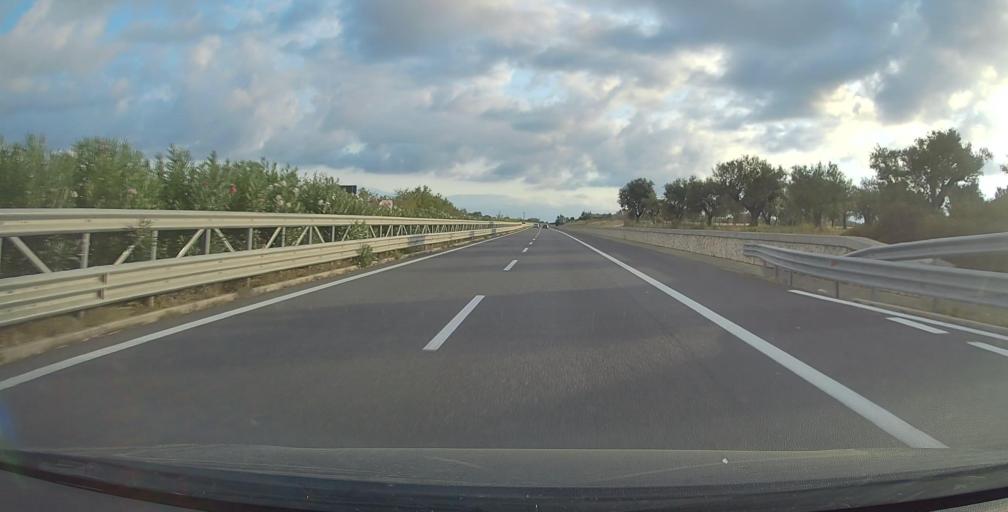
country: IT
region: Calabria
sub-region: Provincia di Catanzaro
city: Acconia
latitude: 38.8294
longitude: 16.2544
